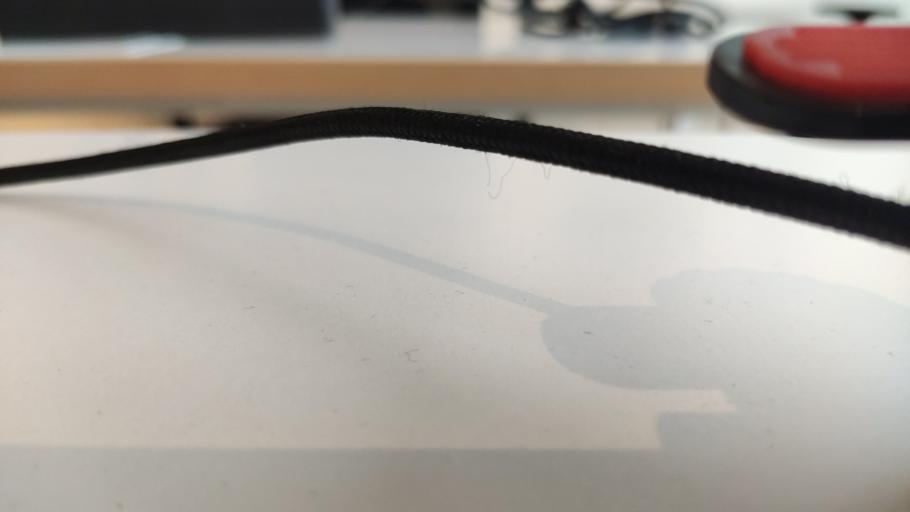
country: RU
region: Moskovskaya
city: Klin
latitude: 56.3436
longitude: 36.7471
